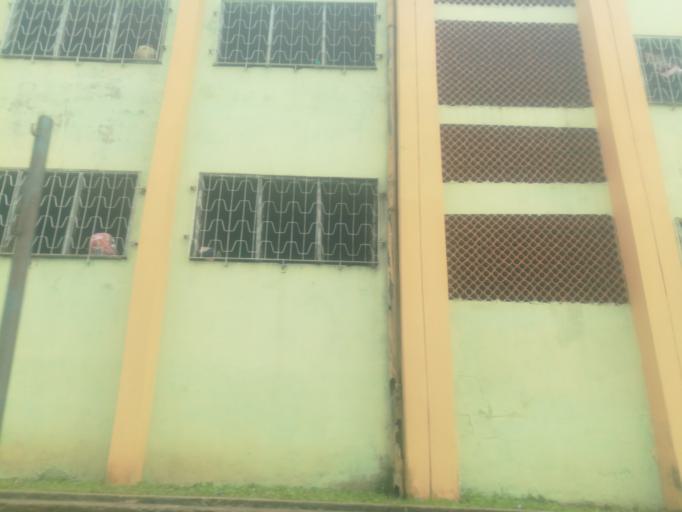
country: NG
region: Oyo
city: Ibadan
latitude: 7.3867
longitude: 3.9339
